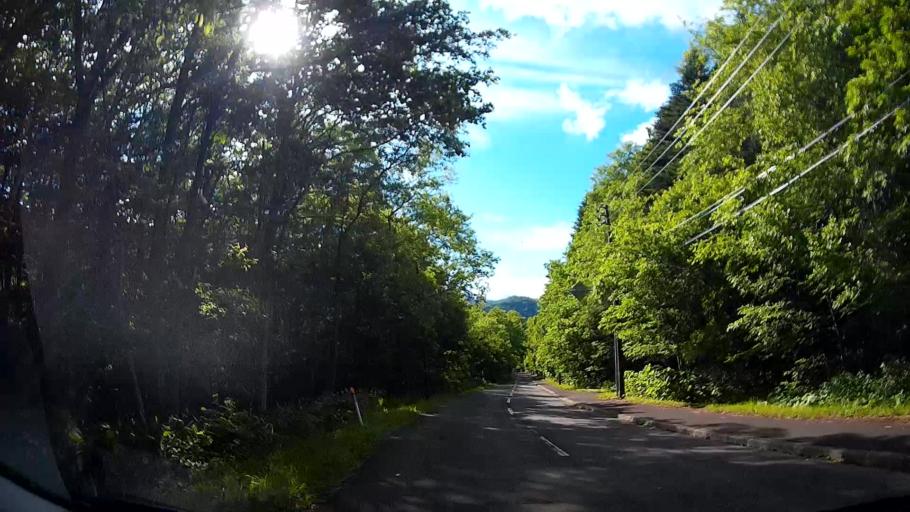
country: JP
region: Hokkaido
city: Sapporo
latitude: 42.9329
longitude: 141.1593
